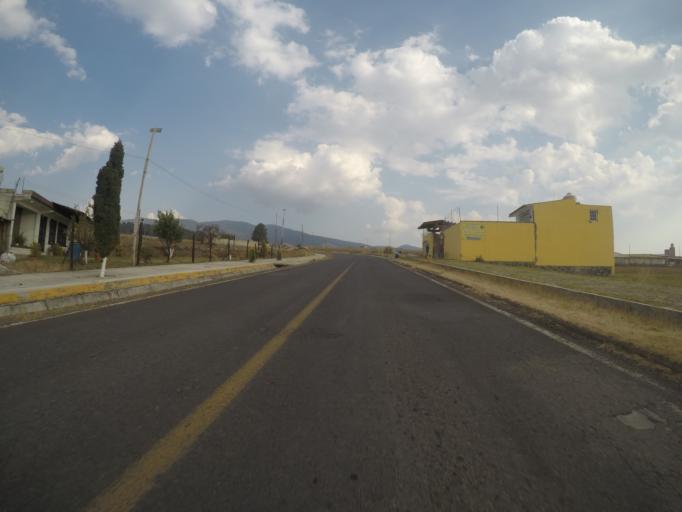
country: MX
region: Mexico
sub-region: Xalatlaco
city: El Aguila (La Mesa)
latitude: 19.1601
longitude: -99.4046
